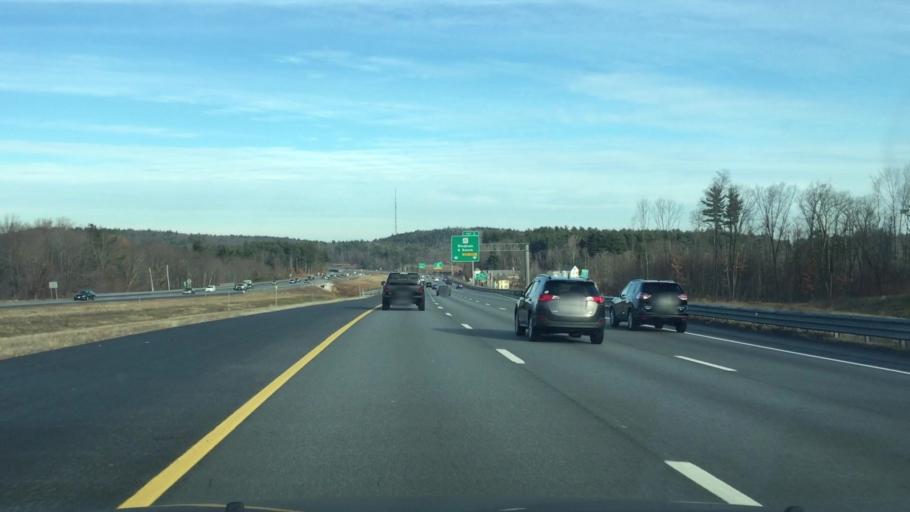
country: US
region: New Hampshire
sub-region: Rockingham County
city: Windham
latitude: 42.7967
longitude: -71.2717
